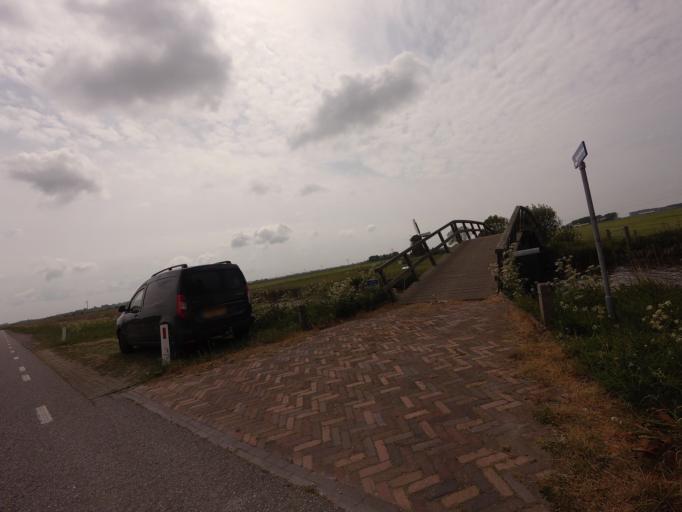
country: NL
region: Friesland
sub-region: Sudwest Fryslan
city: Bolsward
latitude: 53.1028
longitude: 5.5133
